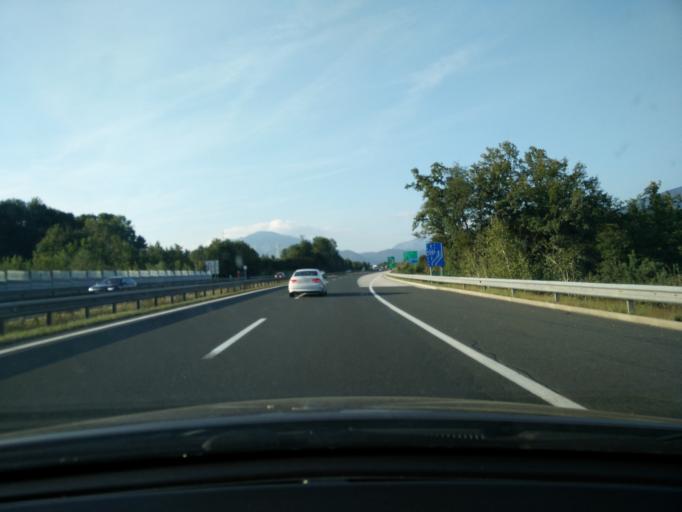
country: SI
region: Naklo
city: Naklo
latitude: 46.2947
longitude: 14.2842
